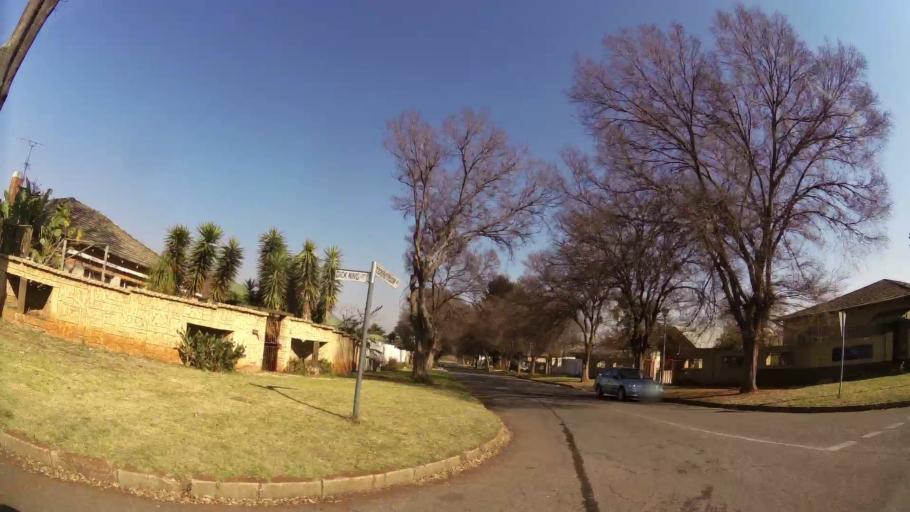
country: ZA
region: Gauteng
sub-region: Ekurhuleni Metropolitan Municipality
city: Boksburg
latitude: -26.2273
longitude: 28.2700
